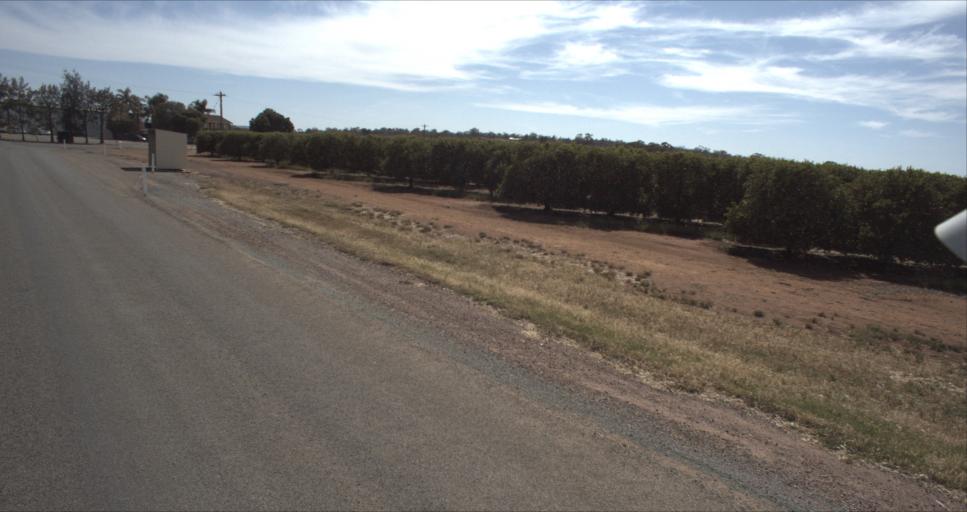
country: AU
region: New South Wales
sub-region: Leeton
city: Leeton
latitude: -34.5888
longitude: 146.4730
